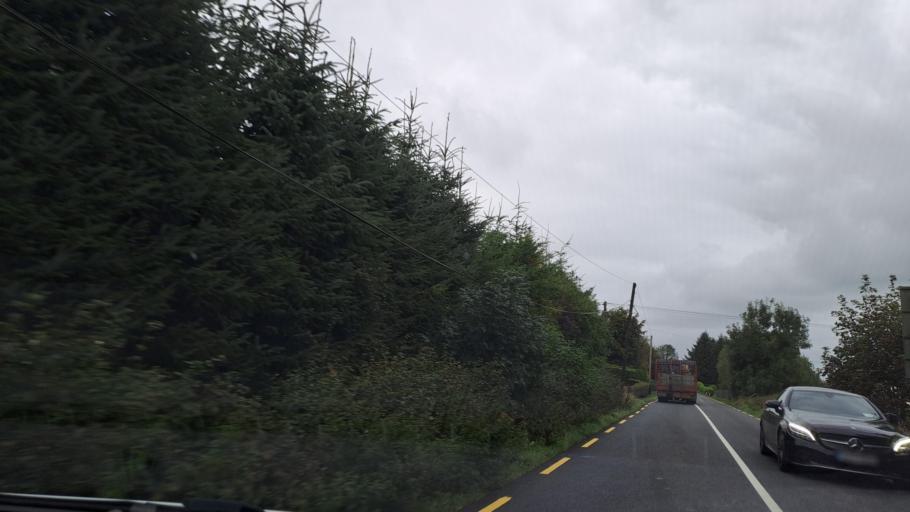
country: IE
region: Ulster
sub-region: County Monaghan
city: Castleblayney
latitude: 54.0852
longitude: -6.8270
